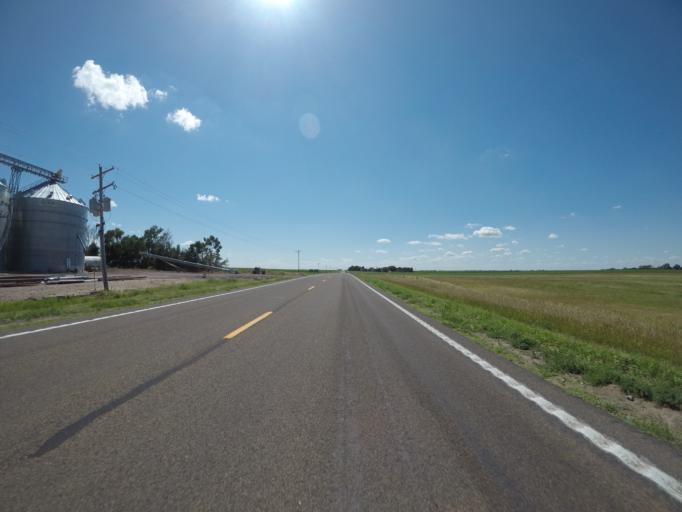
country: US
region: Nebraska
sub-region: Chase County
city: Imperial
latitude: 40.5377
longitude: -101.6675
